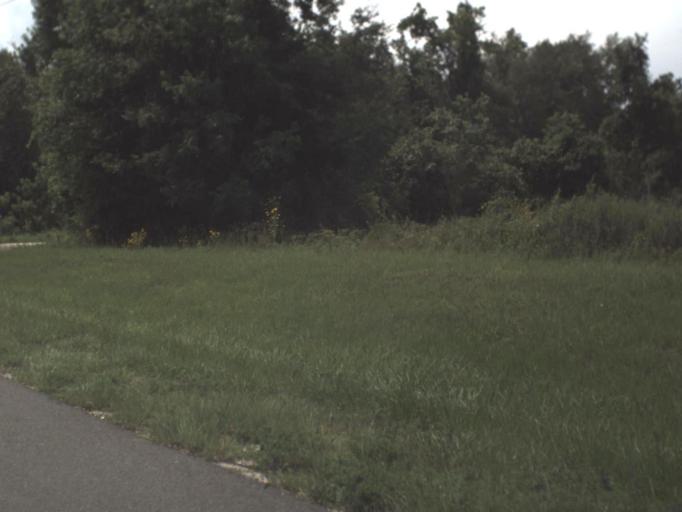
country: US
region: Florida
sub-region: Clay County
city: Keystone Heights
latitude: 29.8028
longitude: -82.0593
